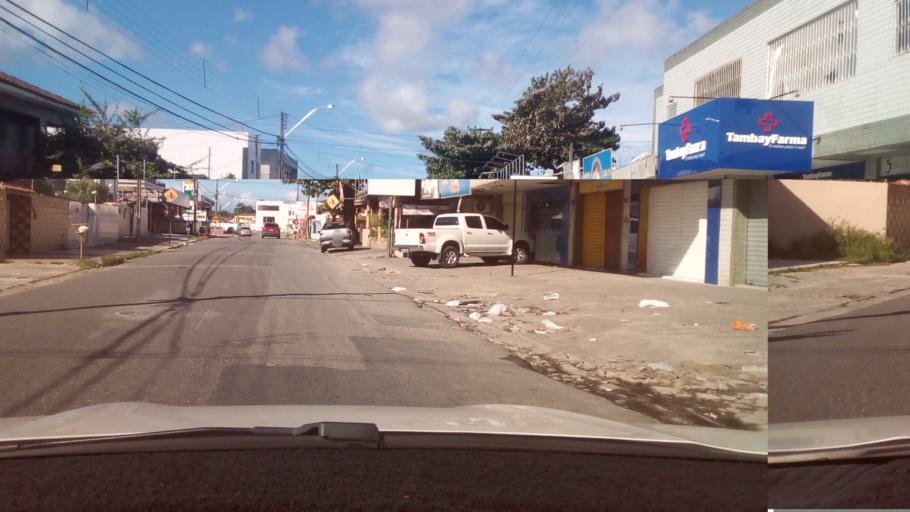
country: BR
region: Paraiba
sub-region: Joao Pessoa
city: Joao Pessoa
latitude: -7.1563
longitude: -34.8735
